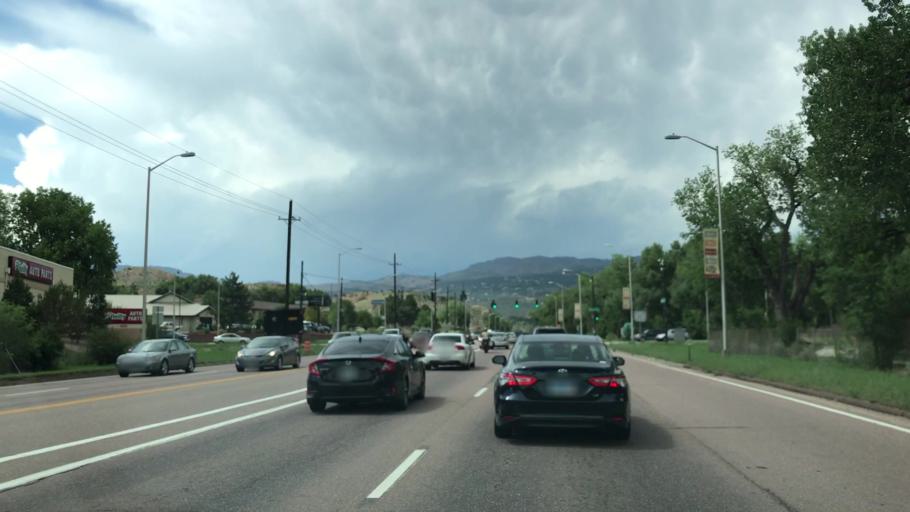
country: US
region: Colorado
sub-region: El Paso County
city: Colorado Springs
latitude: 38.8450
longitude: -104.8656
